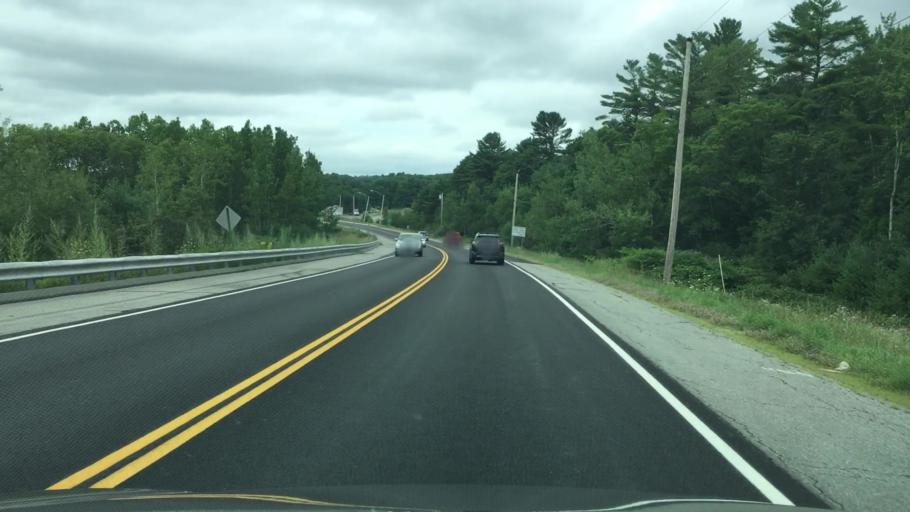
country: US
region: Maine
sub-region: Penobscot County
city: Orrington
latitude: 44.6915
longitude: -68.8112
